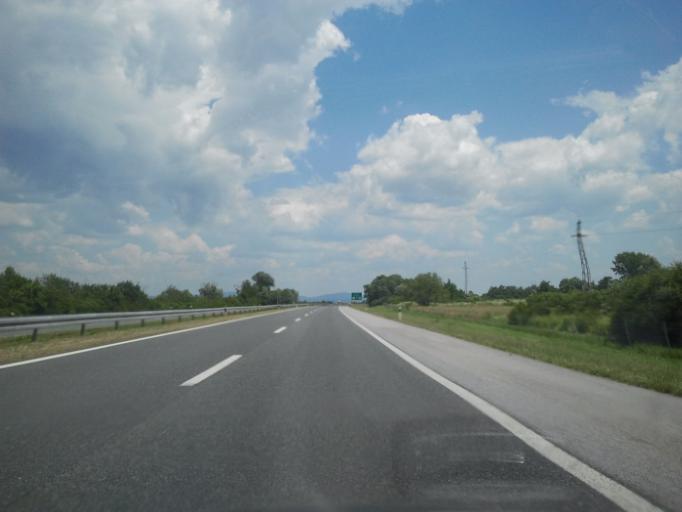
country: HR
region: Brodsko-Posavska
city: Okucani
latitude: 45.2307
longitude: 17.2487
